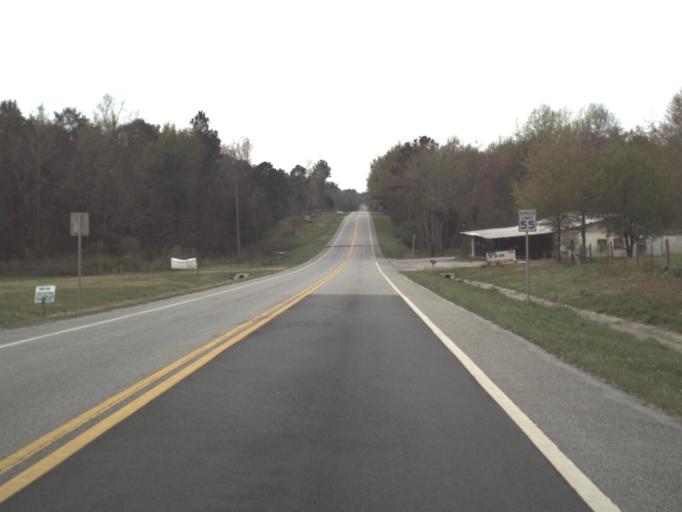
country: US
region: Florida
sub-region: Jackson County
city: Graceville
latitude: 30.9776
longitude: -85.6465
